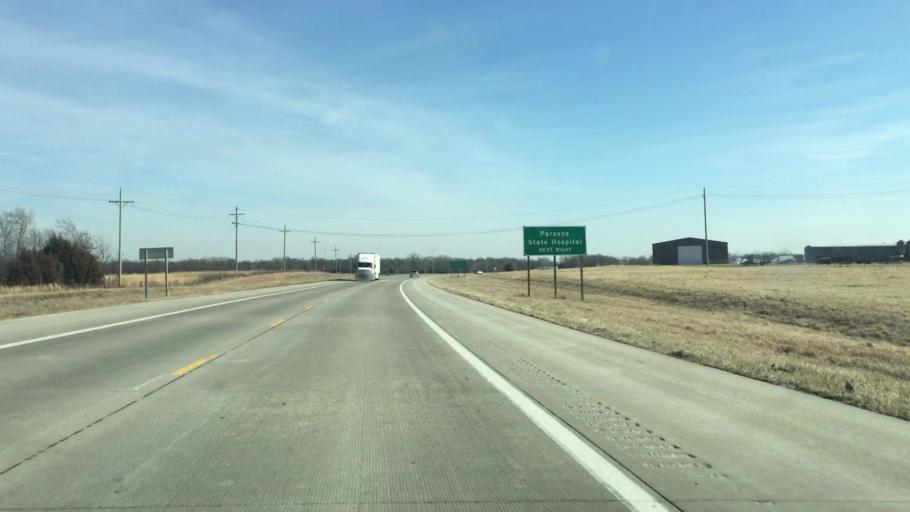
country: US
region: Kansas
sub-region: Labette County
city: Parsons
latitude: 37.3689
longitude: -95.2905
